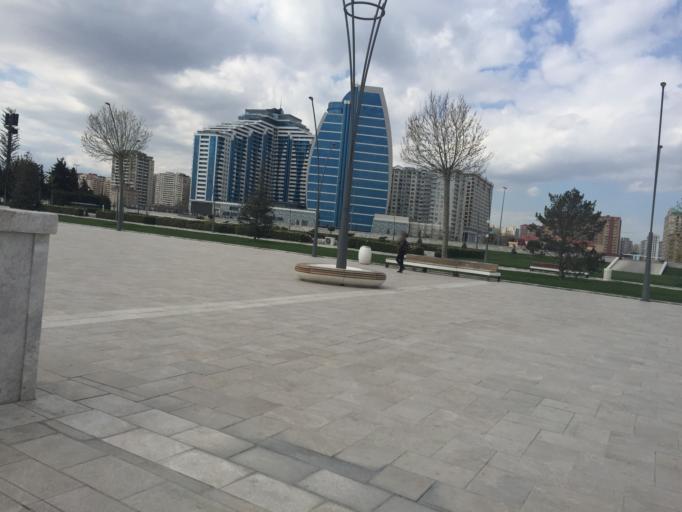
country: AZ
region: Baki
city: Baku
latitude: 40.3748
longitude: 49.8782
